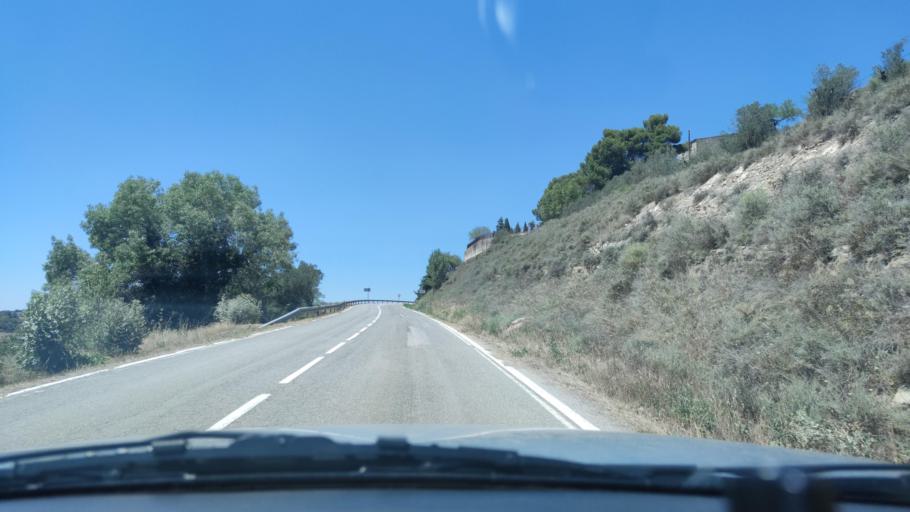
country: ES
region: Catalonia
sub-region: Provincia de Lleida
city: Ivorra
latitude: 41.7697
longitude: 1.3959
